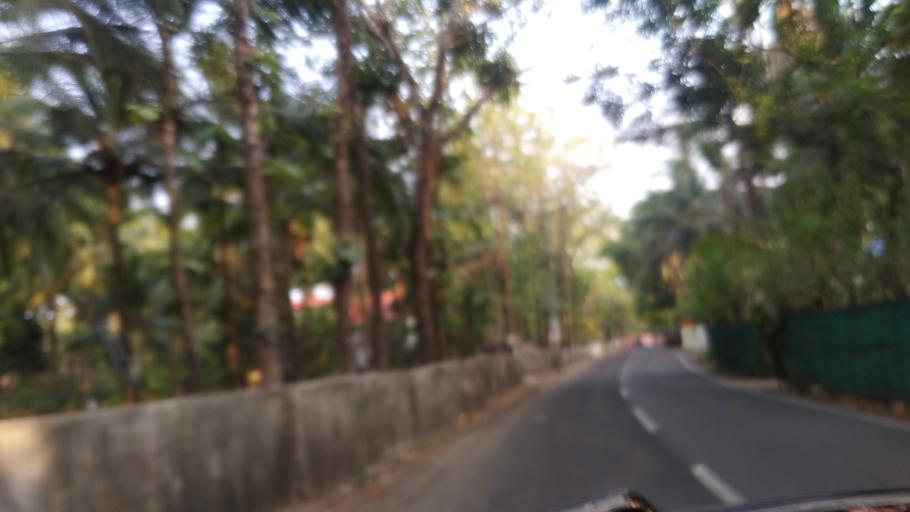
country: IN
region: Kerala
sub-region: Thrissur District
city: Thanniyam
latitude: 10.4047
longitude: 76.0955
